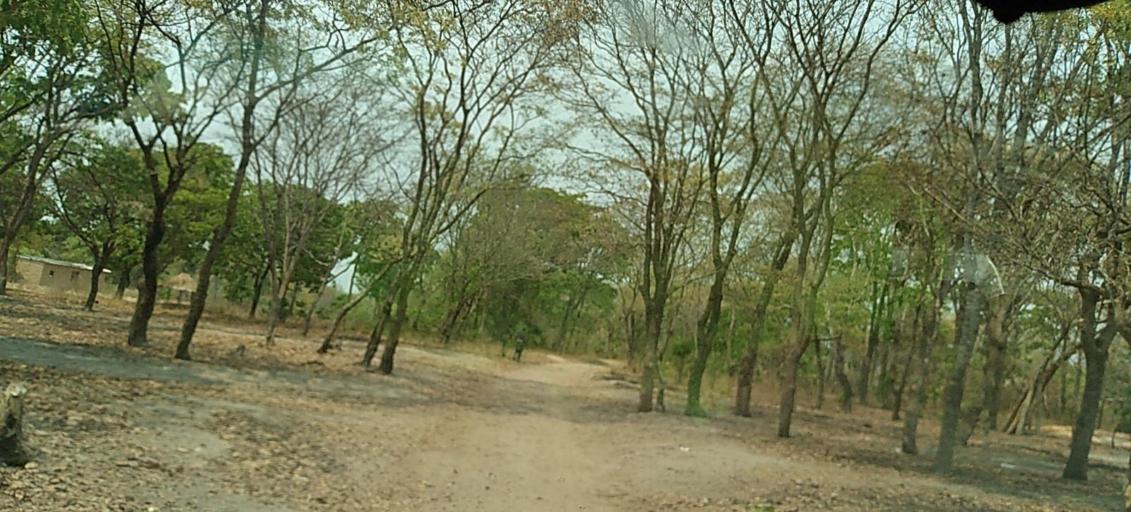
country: ZM
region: North-Western
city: Kabompo
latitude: -13.5408
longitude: 24.4520
